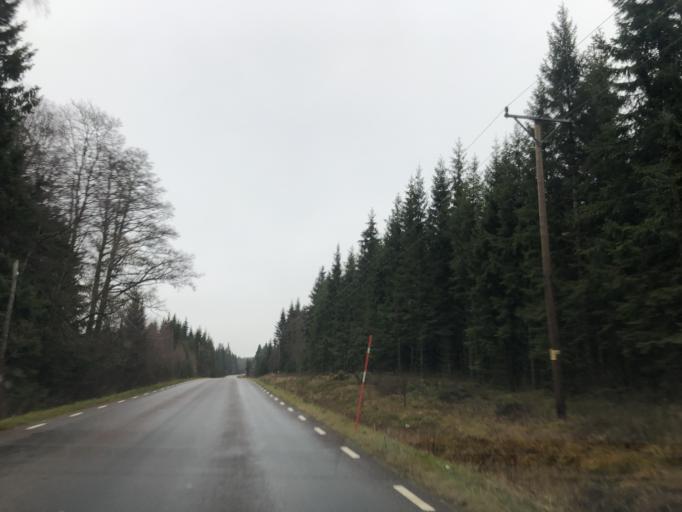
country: SE
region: Vaestra Goetaland
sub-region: Ulricehamns Kommun
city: Ulricehamn
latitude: 57.7496
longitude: 13.5226
